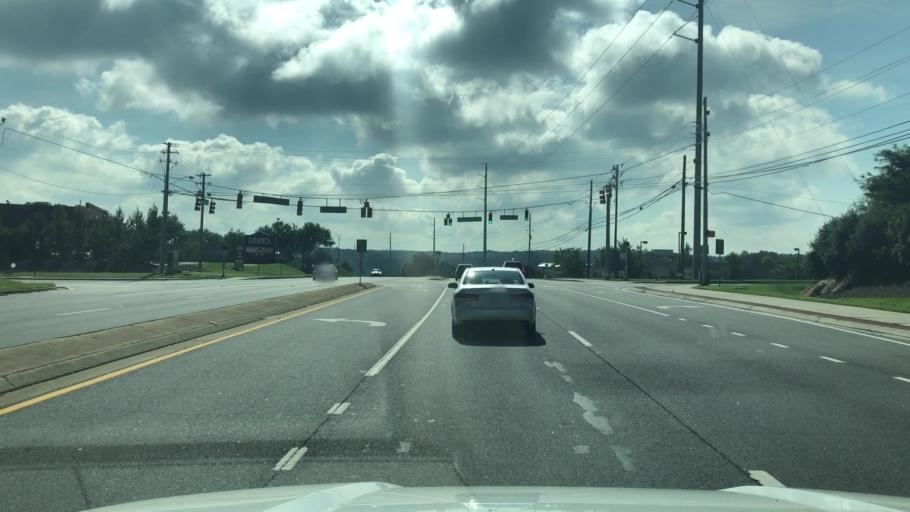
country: US
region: Georgia
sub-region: Cobb County
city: Kennesaw
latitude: 33.9471
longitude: -84.6312
